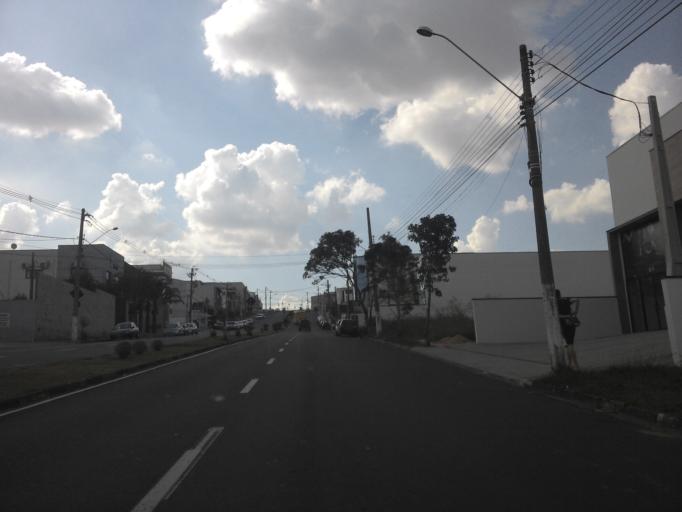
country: BR
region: Sao Paulo
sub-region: Valinhos
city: Valinhos
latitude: -22.9854
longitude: -47.0129
